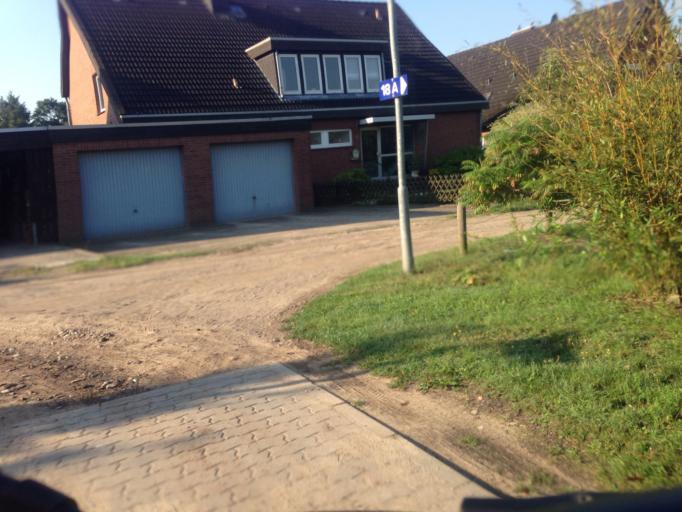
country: DE
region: Lower Saxony
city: Adendorf
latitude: 53.2818
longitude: 10.4288
